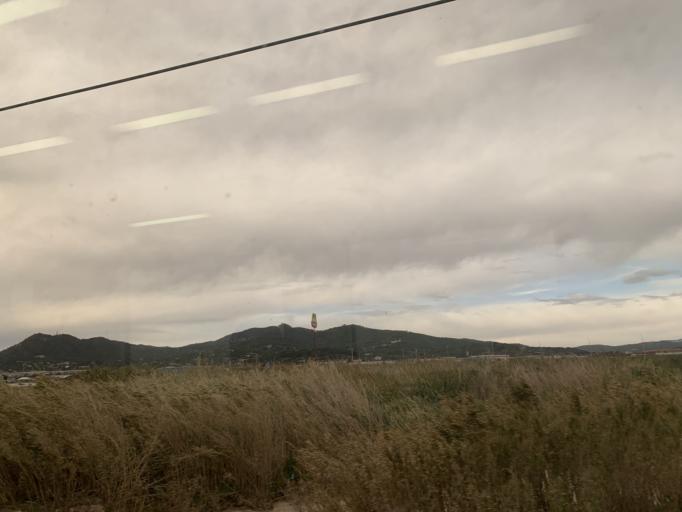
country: ES
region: Catalonia
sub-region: Provincia de Barcelona
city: Cabrera de Mar
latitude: 41.5197
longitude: 2.4245
